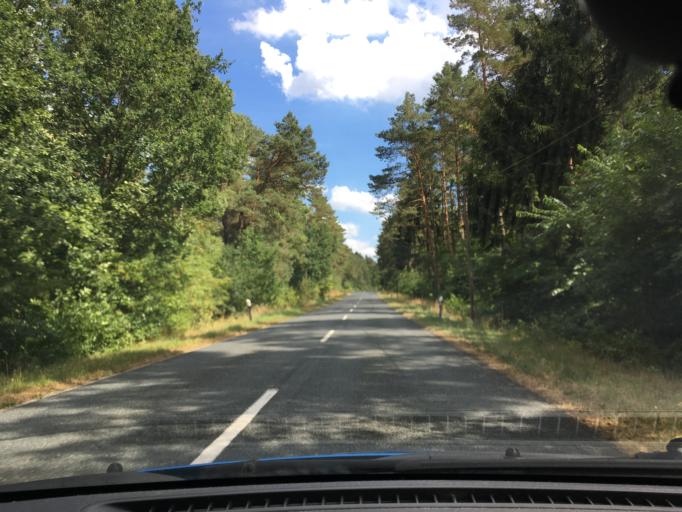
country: DE
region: Lower Saxony
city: Rehlingen
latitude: 53.0831
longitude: 10.2160
